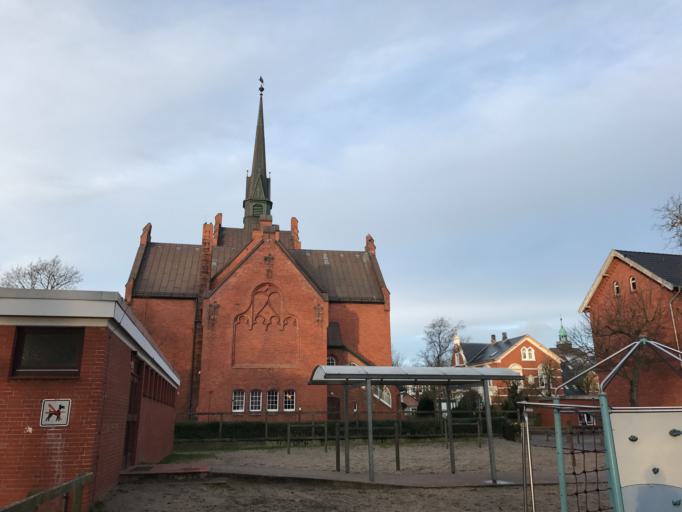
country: DE
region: Lower Saxony
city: Borkum
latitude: 53.5868
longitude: 6.6697
